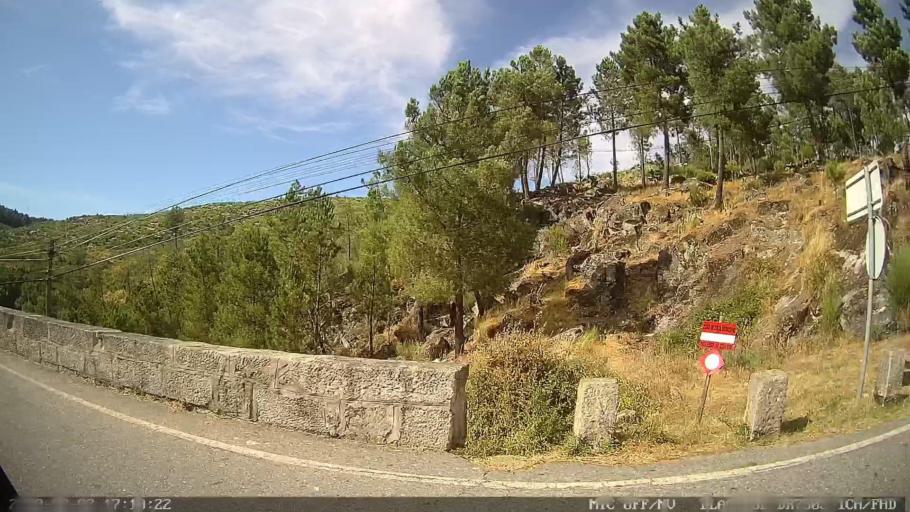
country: PT
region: Vila Real
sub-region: Sabrosa
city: Sabrosa
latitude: 41.3523
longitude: -7.5915
